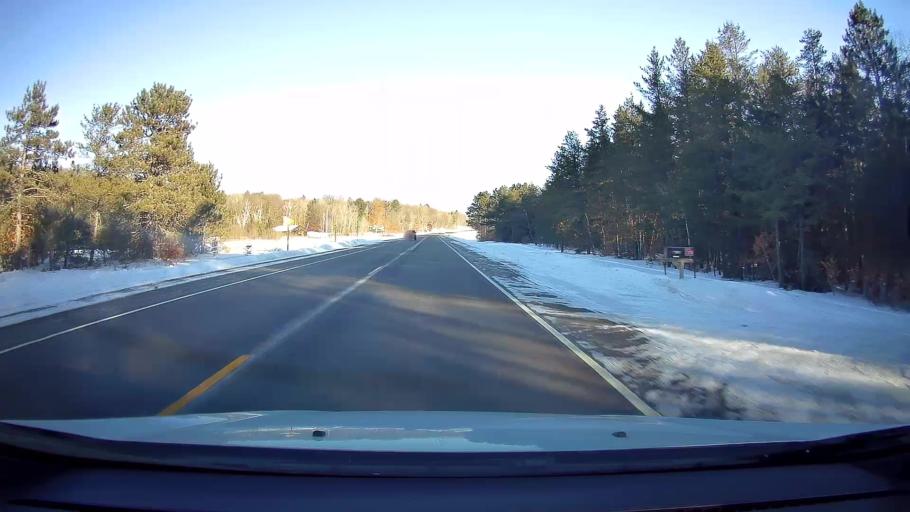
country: US
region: Wisconsin
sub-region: Sawyer County
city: Hayward
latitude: 46.0563
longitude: -91.4407
